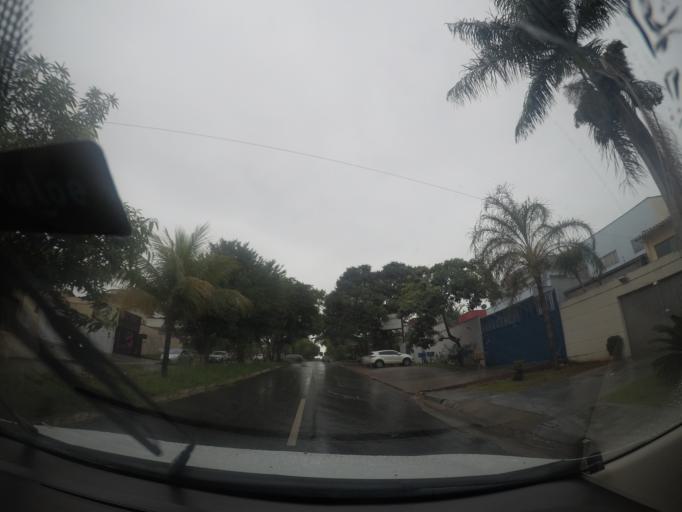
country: BR
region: Goias
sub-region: Goiania
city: Goiania
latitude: -16.6448
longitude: -49.2284
